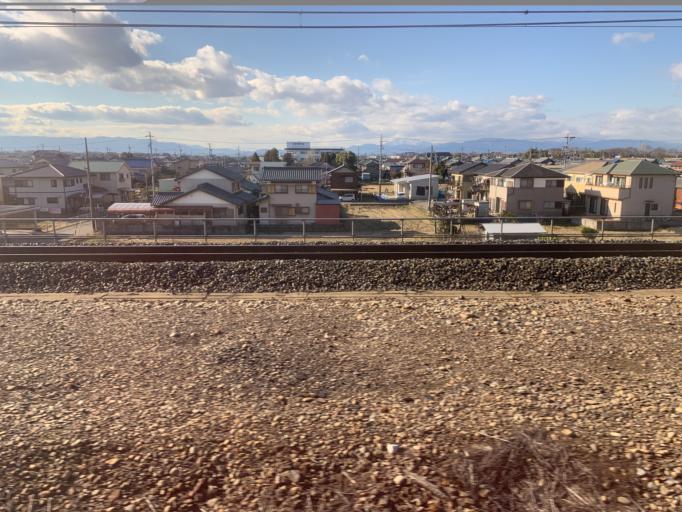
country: JP
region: Gifu
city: Kasamatsucho
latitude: 35.3644
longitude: 136.7797
